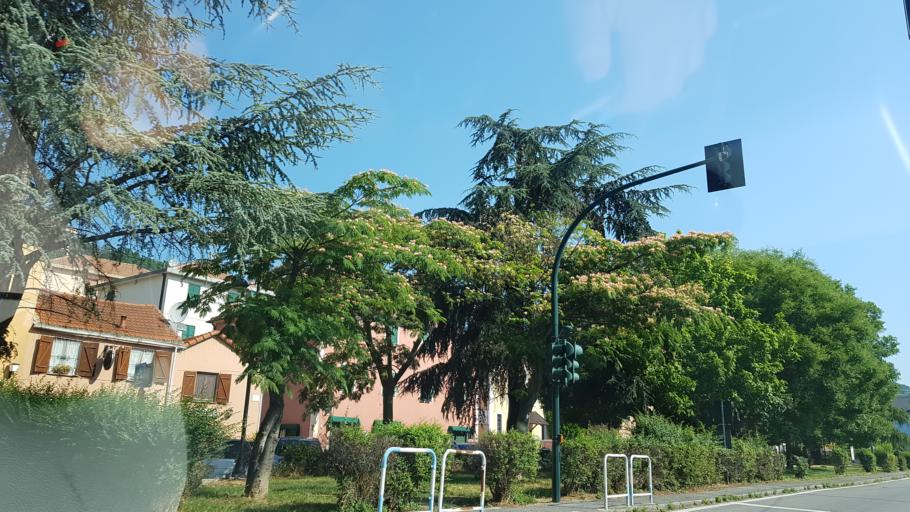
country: IT
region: Liguria
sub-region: Provincia di Genova
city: Pedemonte
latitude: 44.4970
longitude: 8.9214
